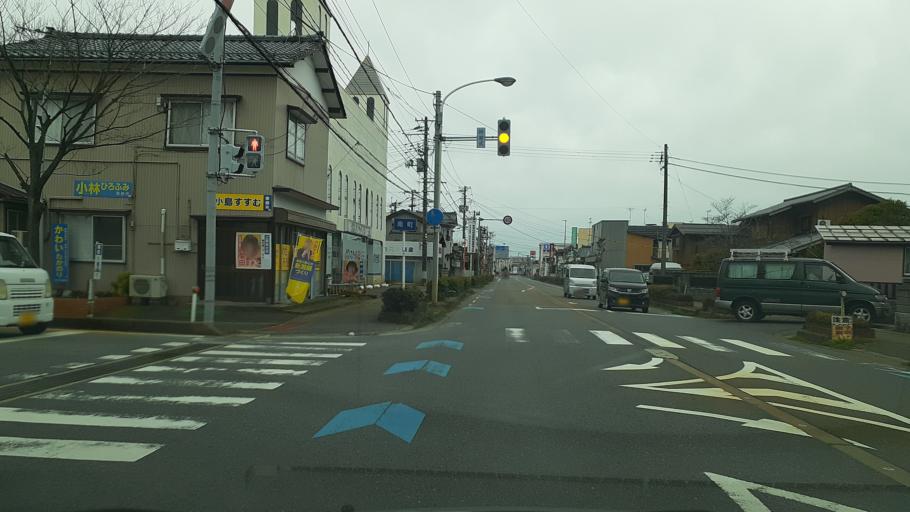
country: JP
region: Niigata
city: Niitsu-honcho
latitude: 37.7946
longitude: 139.1176
